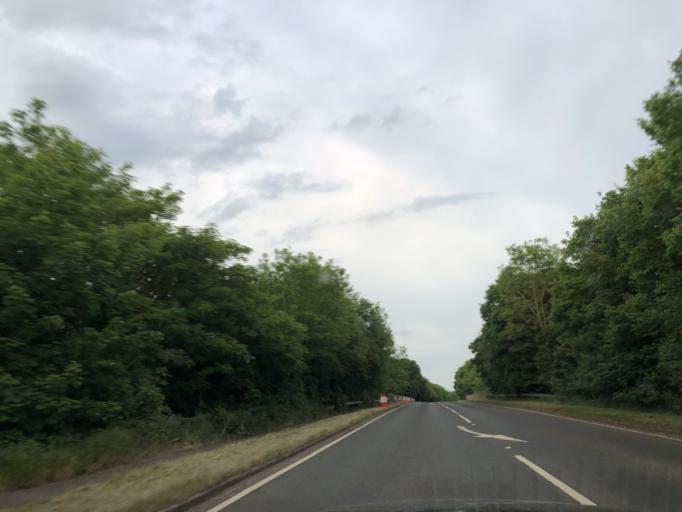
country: GB
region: England
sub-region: Warwickshire
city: Warwick
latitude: 52.2746
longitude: -1.6156
